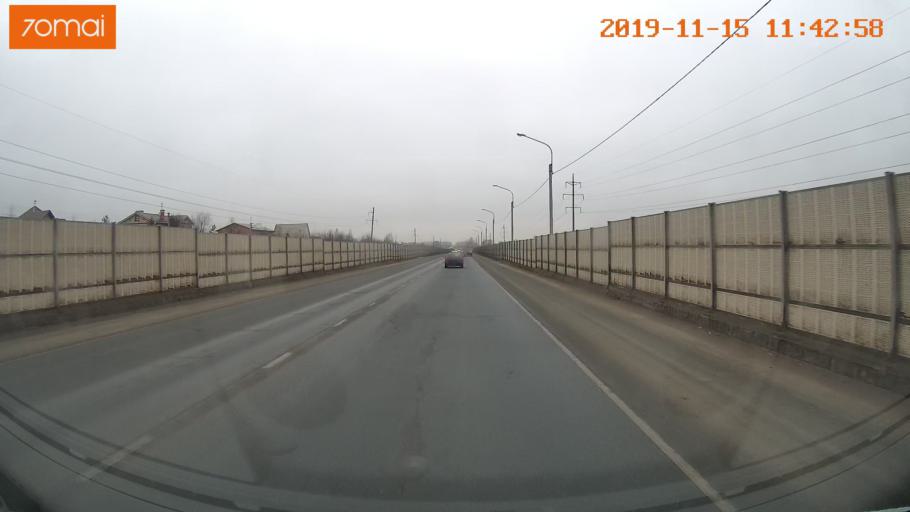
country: RU
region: Vologda
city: Vologda
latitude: 59.2236
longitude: 39.7751
